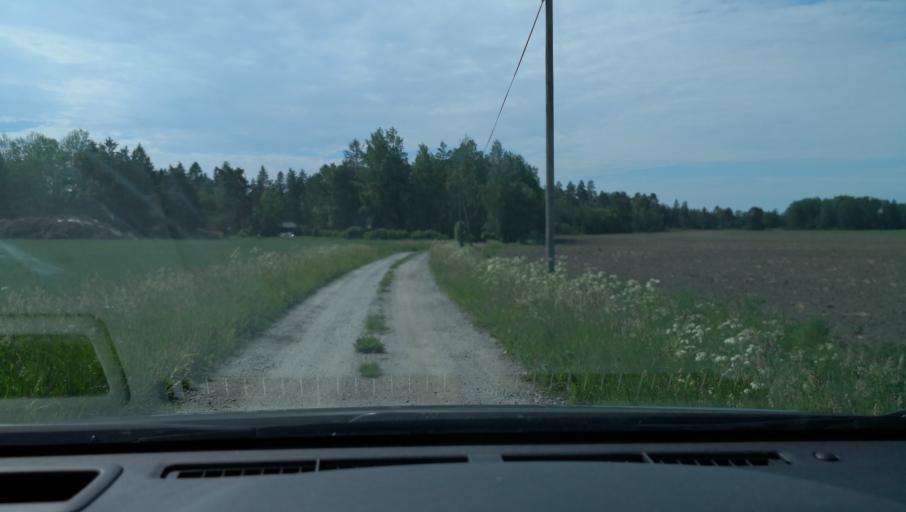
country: SE
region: Uppsala
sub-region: Enkopings Kommun
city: Enkoping
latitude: 59.7035
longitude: 17.1392
